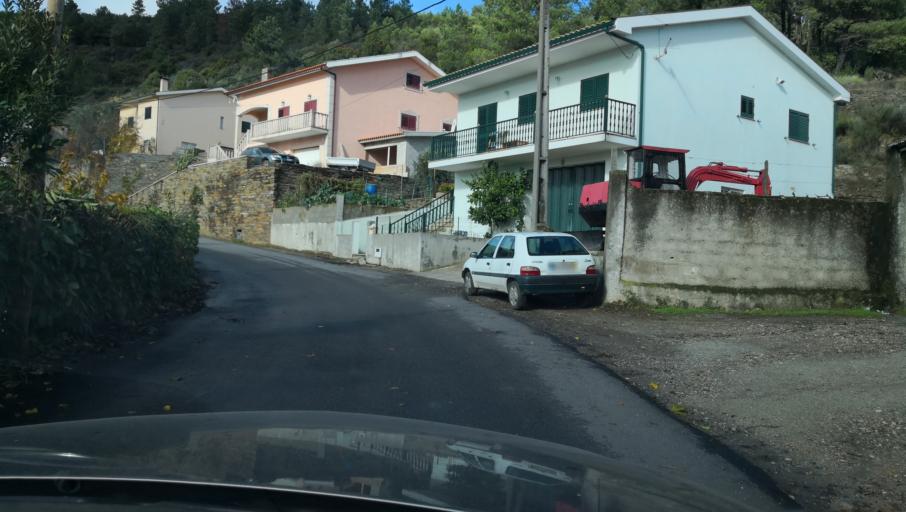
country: PT
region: Vila Real
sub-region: Sabrosa
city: Vilela
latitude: 41.2209
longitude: -7.5742
